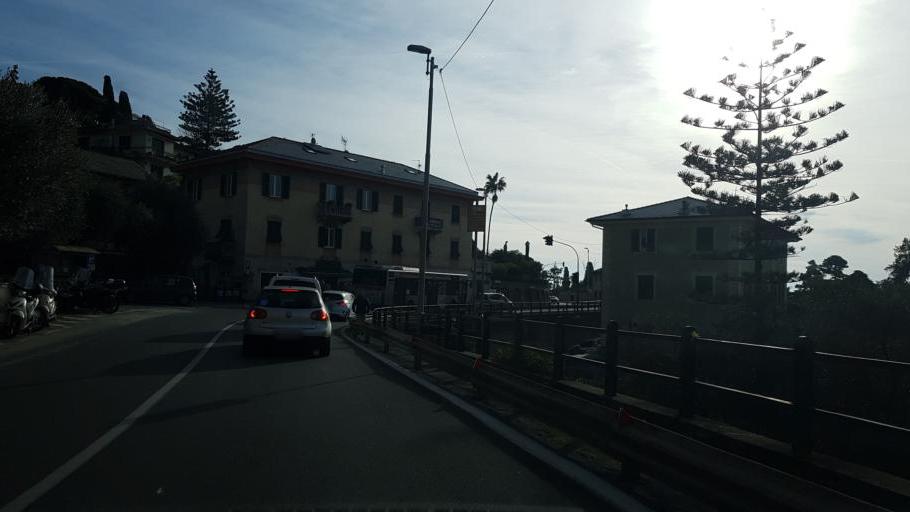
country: IT
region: Liguria
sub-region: Provincia di Genova
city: Pieve Ligure
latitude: 44.3749
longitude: 9.0847
